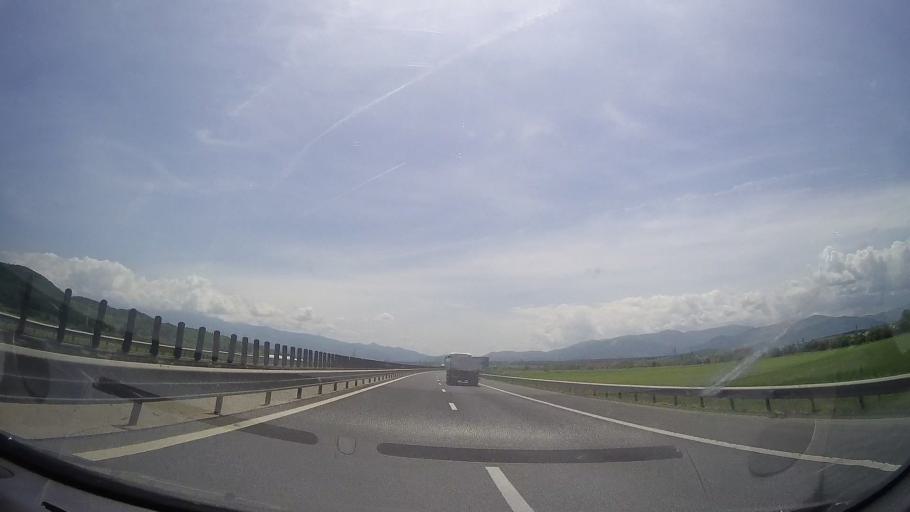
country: RO
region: Sibiu
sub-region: Comuna Selimbar
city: Selimbar
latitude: 45.7688
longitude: 24.2058
